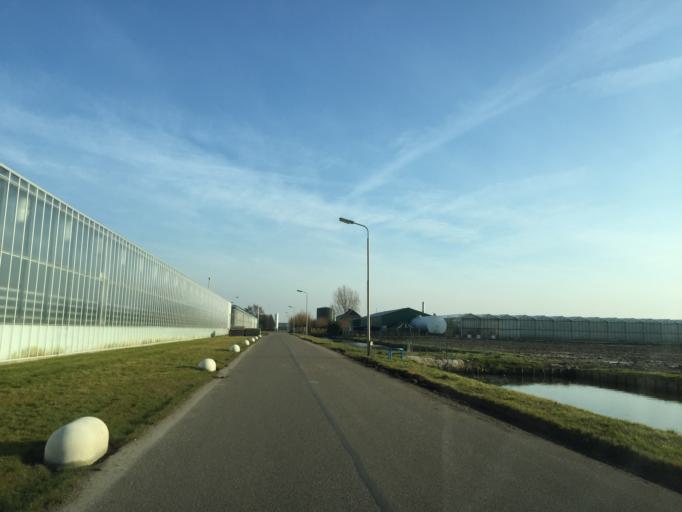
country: NL
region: South Holland
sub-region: Gemeente Pijnacker-Nootdorp
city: Pijnacker
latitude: 52.0191
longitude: 4.4045
